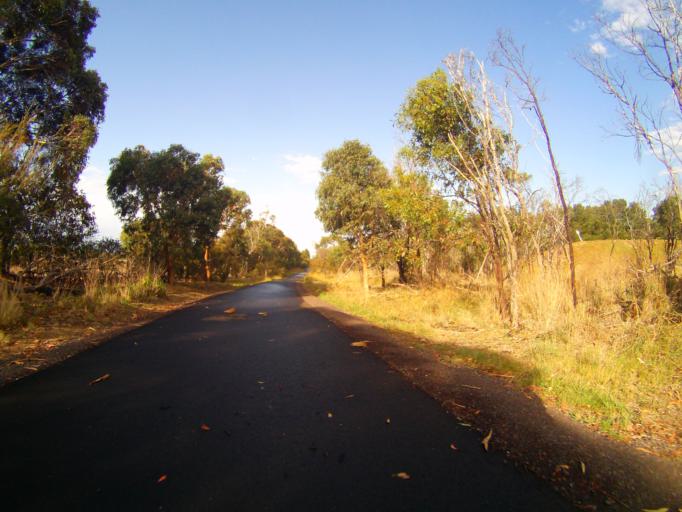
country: AU
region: Victoria
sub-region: Greater Geelong
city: Clifton Springs
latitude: -38.1804
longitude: 144.5217
